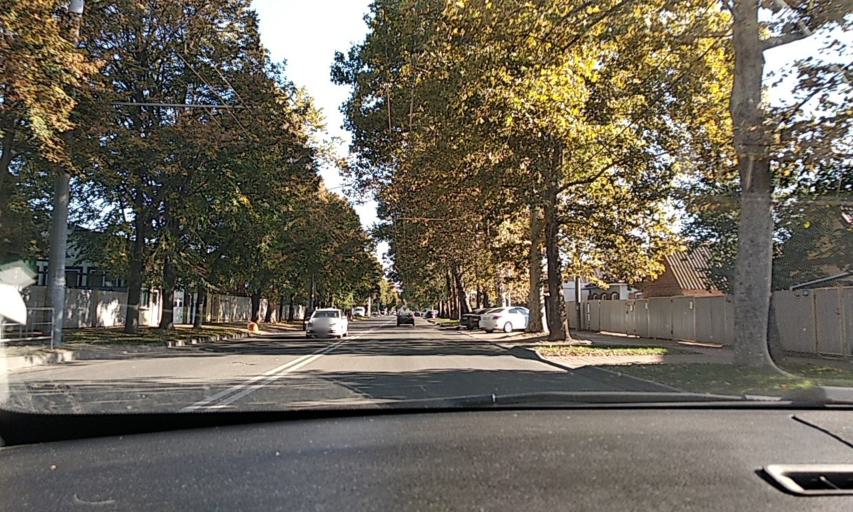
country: RU
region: Krasnodarskiy
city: Pashkovskiy
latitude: 45.0245
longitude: 39.1133
